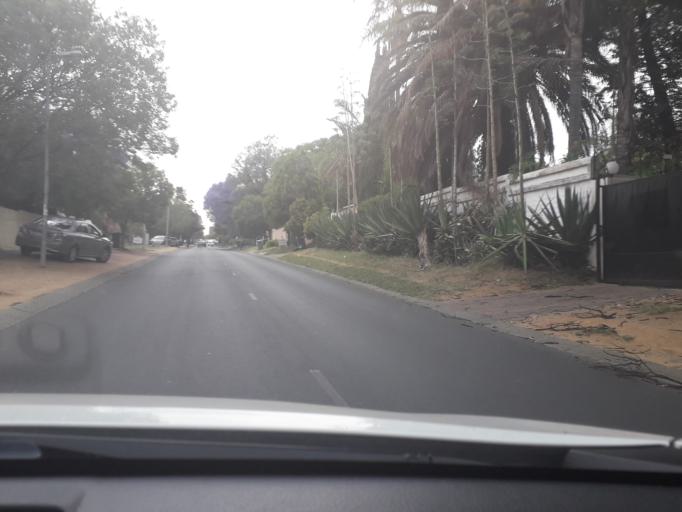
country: ZA
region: Gauteng
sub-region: City of Johannesburg Metropolitan Municipality
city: Johannesburg
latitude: -26.0881
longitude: 27.9941
